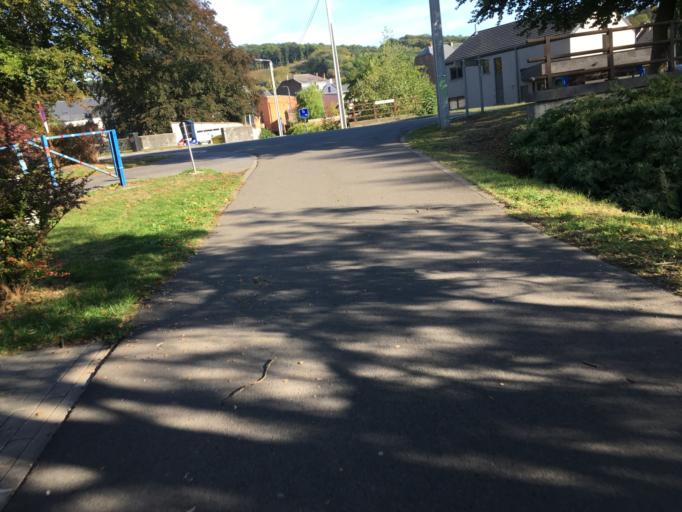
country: BE
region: Wallonia
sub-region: Province de Namur
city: Floreffe
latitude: 50.4366
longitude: 4.7585
